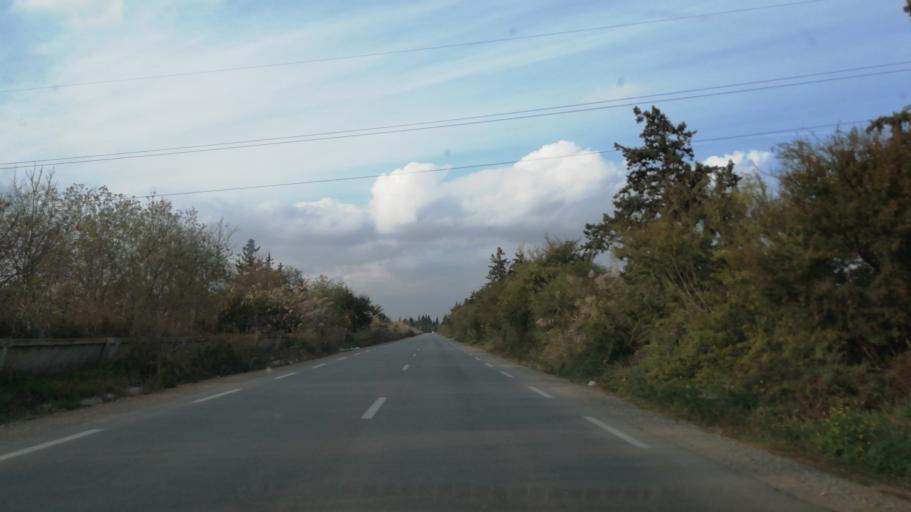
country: DZ
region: Mascara
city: Mascara
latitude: 35.6271
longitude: 0.0425
